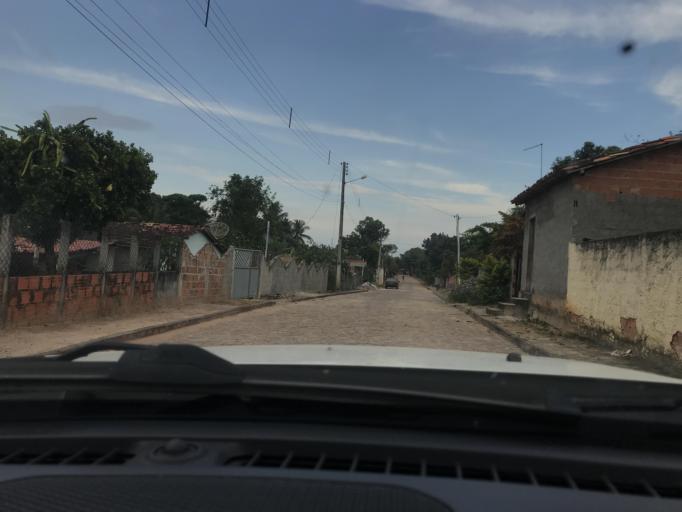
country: BR
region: Bahia
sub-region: Entre Rios
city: Entre Rios
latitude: -12.0121
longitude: -38.2168
